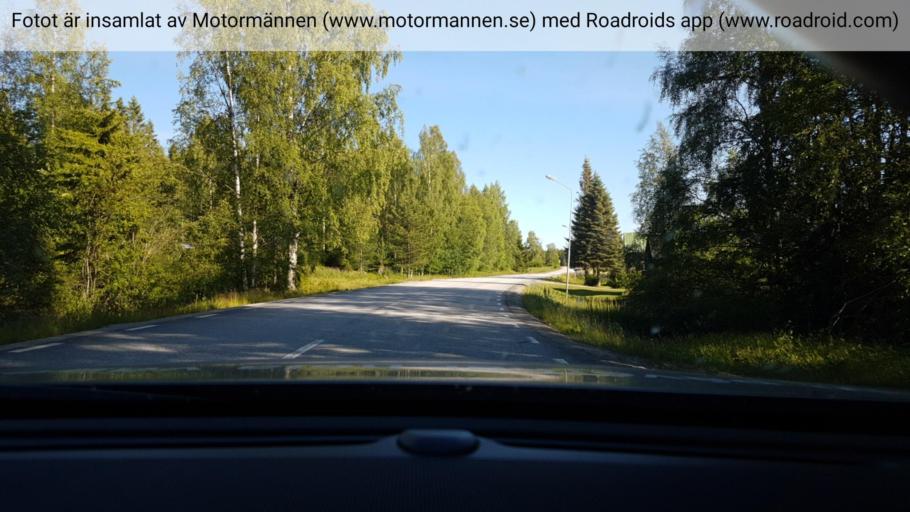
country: SE
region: Vaesterbotten
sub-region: Vindelns Kommun
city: Vindeln
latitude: 64.1109
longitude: 19.5849
